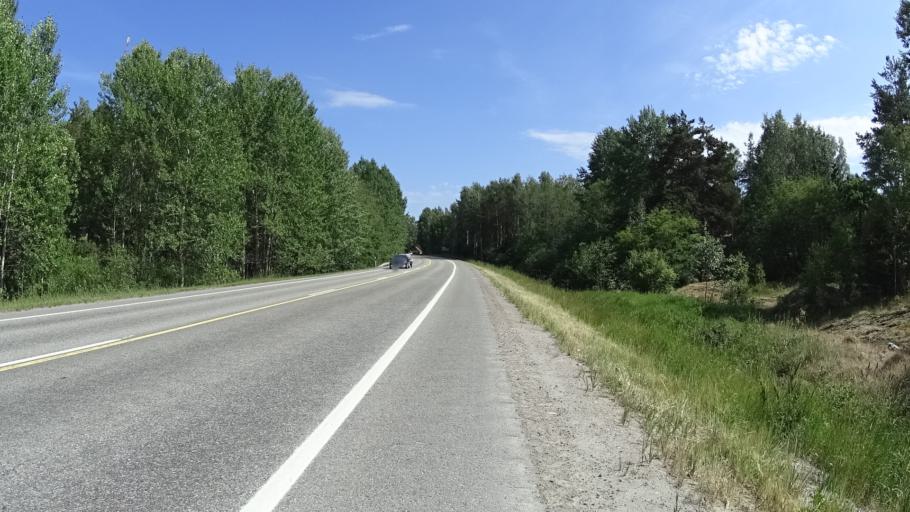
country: FI
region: Uusimaa
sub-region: Raaseporin
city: Karis
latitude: 60.0892
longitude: 23.6456
